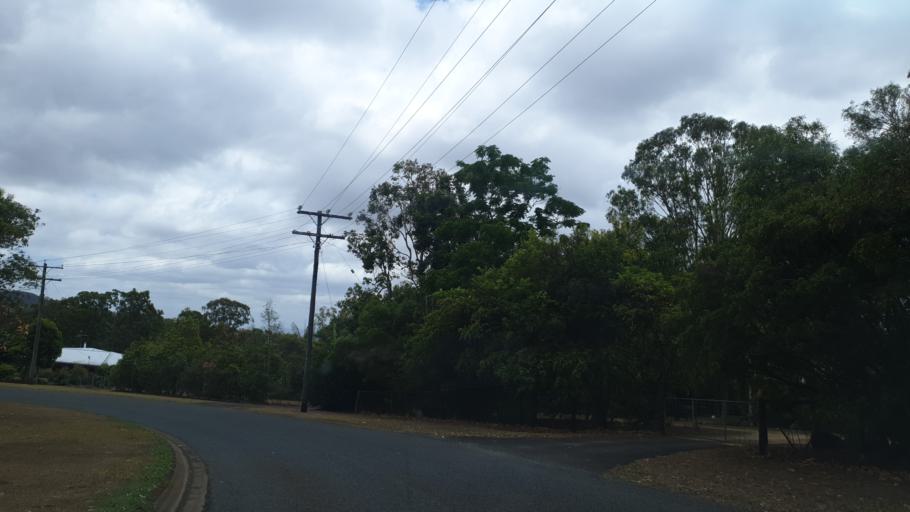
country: AU
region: Queensland
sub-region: Tablelands
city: Tolga
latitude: -17.2079
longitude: 145.4431
